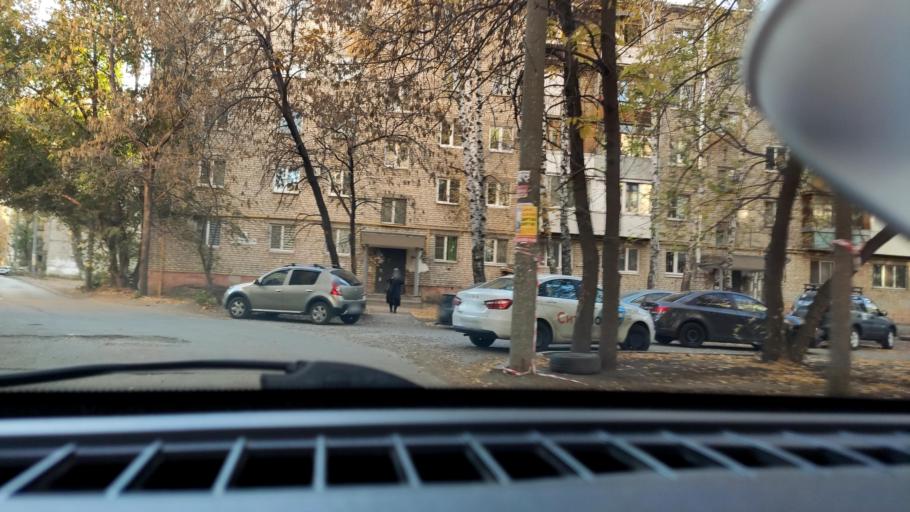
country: RU
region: Samara
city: Smyshlyayevka
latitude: 53.2208
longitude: 50.2742
